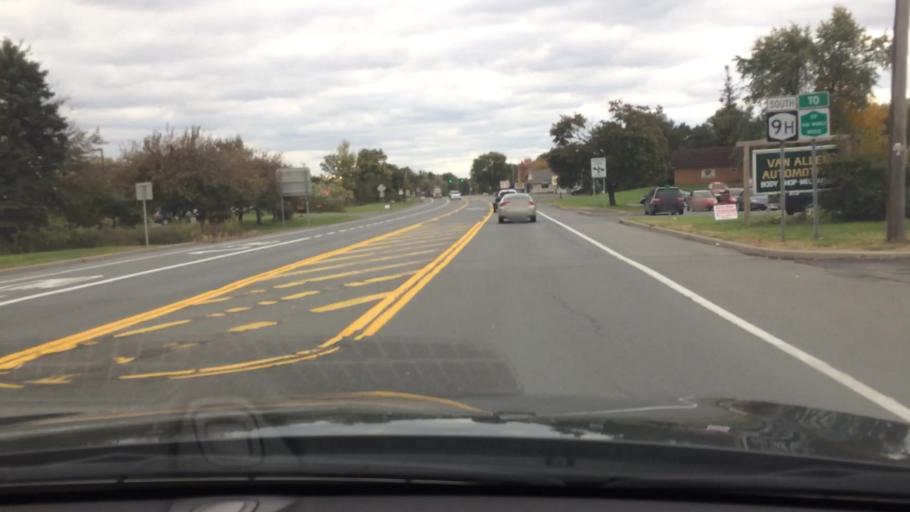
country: US
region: New York
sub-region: Columbia County
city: Valatie
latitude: 42.4275
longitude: -73.6890
